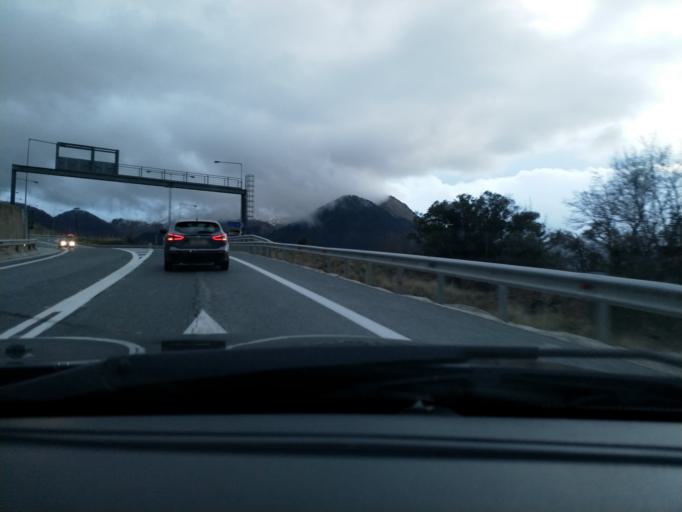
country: GR
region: Epirus
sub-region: Nomos Ioanninon
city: Metsovo
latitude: 39.7622
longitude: 21.1716
